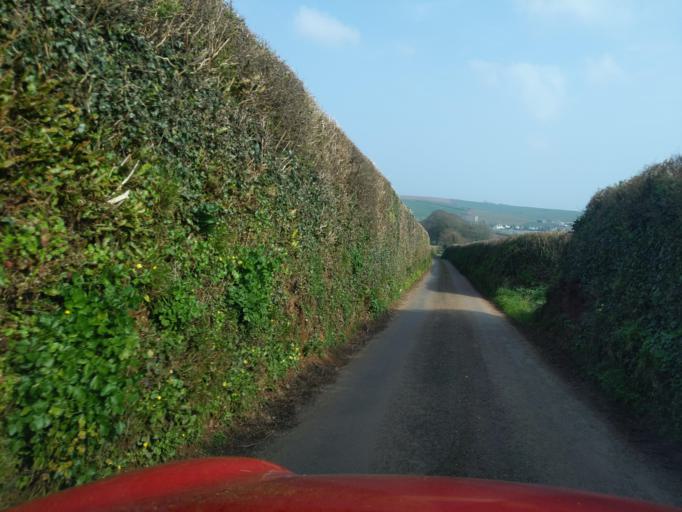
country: GB
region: England
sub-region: Devon
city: Kingsbridge
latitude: 50.2871
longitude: -3.7328
